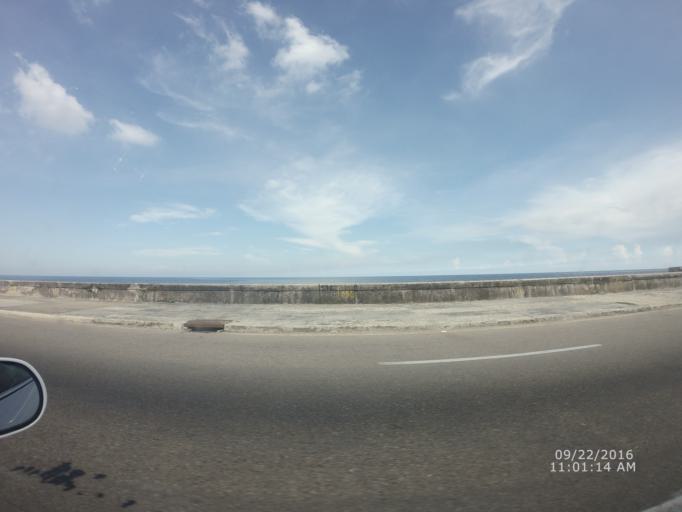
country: CU
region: La Habana
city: Havana
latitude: 23.1389
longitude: -82.4062
